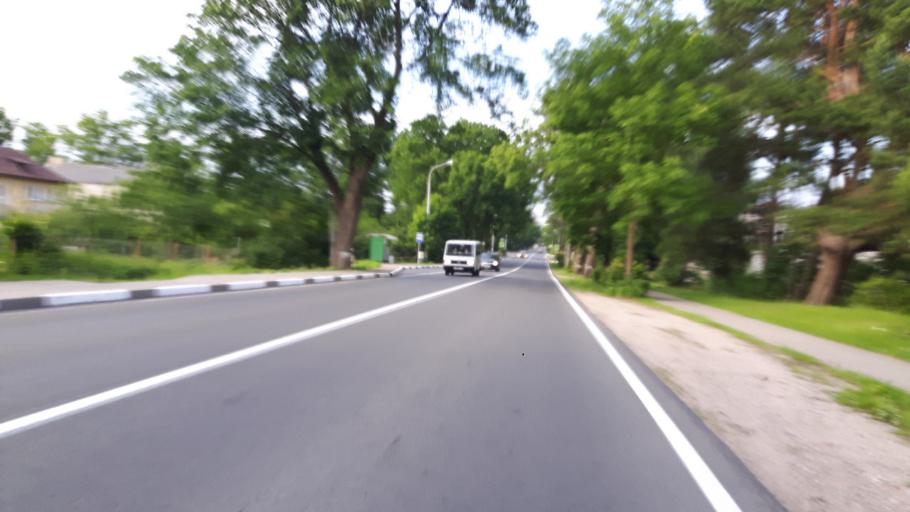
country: RU
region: Kaliningrad
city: Ladushkin
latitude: 54.5647
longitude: 20.1675
